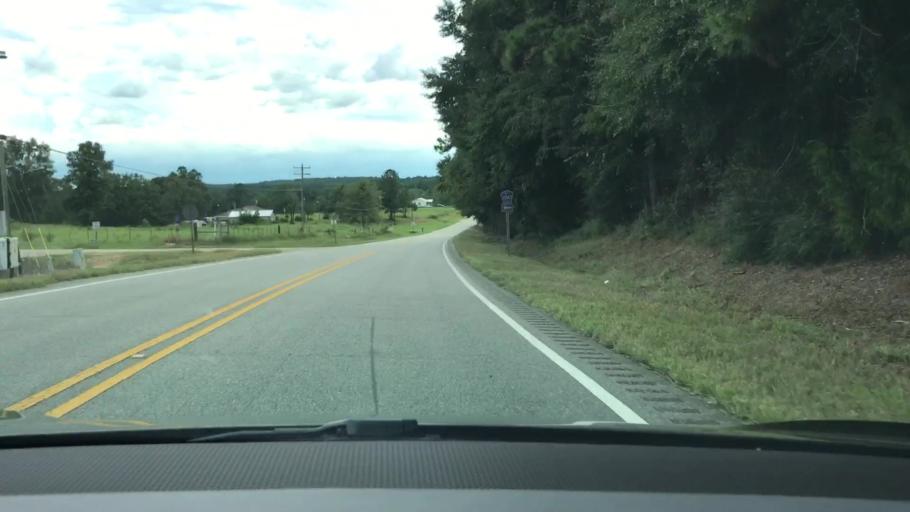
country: US
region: Alabama
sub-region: Pike County
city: Troy
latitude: 31.6616
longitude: -85.9600
